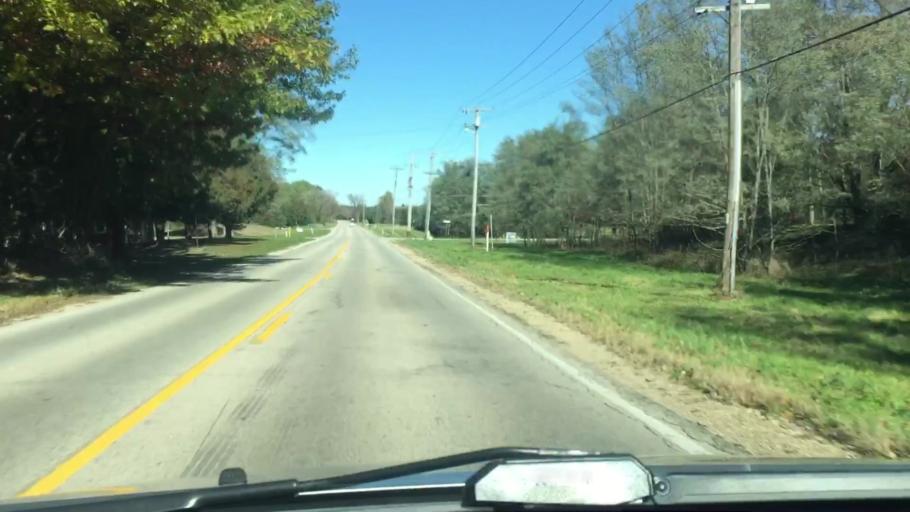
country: US
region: Wisconsin
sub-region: Waukesha County
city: North Prairie
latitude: 42.9585
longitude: -88.4049
